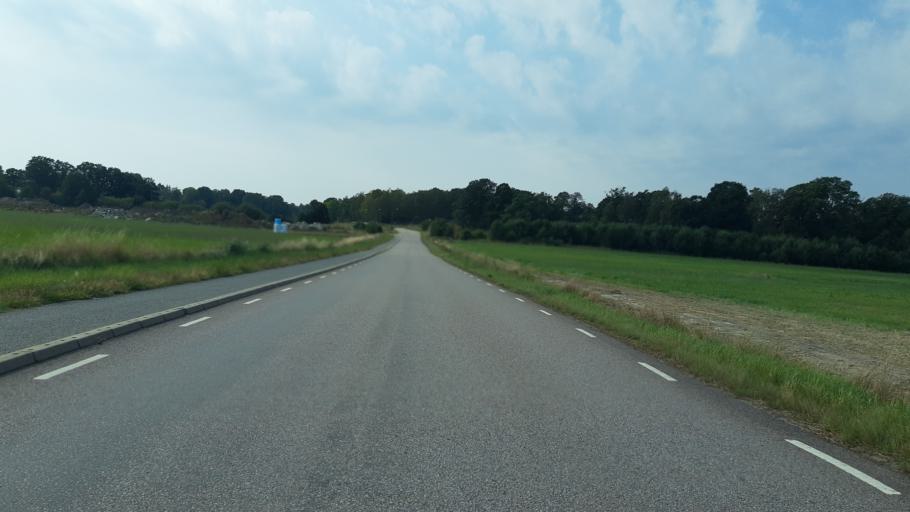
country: SE
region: Blekinge
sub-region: Karlskrona Kommun
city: Nattraby
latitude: 56.1879
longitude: 15.5140
